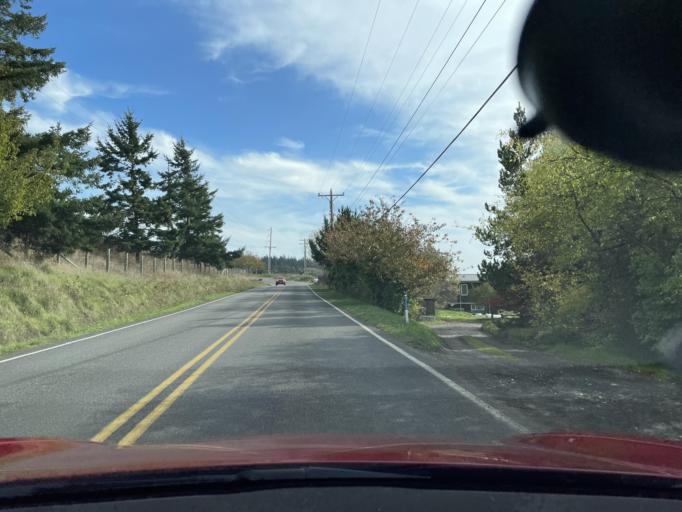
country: US
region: Washington
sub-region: San Juan County
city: Friday Harbor
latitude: 48.5219
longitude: -123.0098
